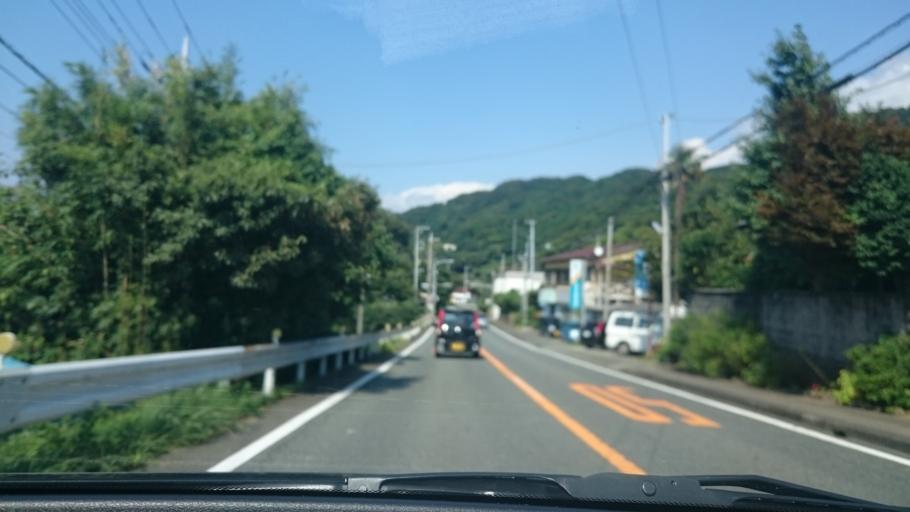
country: JP
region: Shizuoka
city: Heda
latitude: 34.8774
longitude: 138.7602
